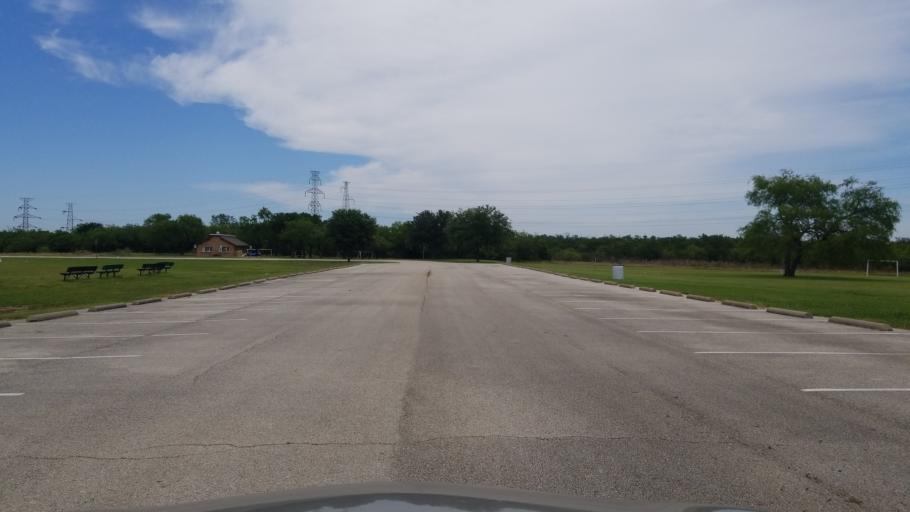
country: US
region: Texas
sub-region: Dallas County
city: Grand Prairie
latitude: 32.6850
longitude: -96.9822
